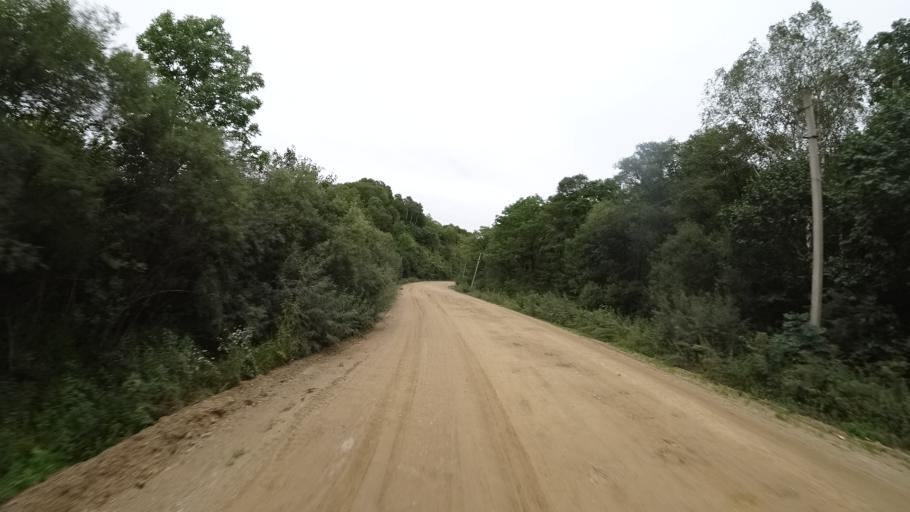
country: RU
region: Primorskiy
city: Rettikhovka
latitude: 44.1789
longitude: 132.8624
